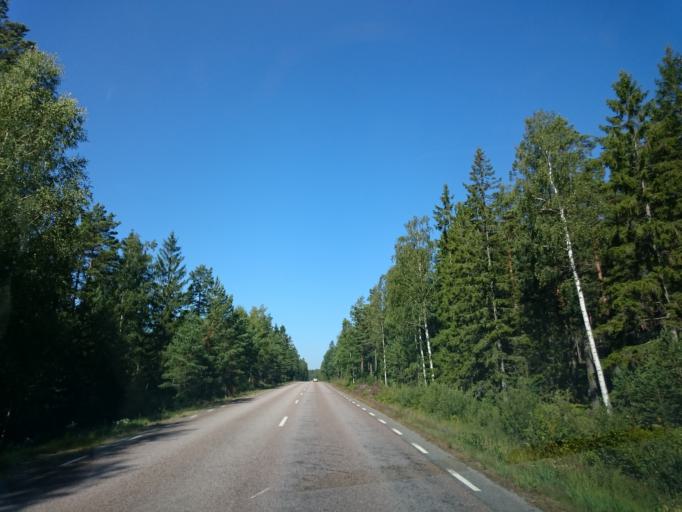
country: SE
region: OEstergoetland
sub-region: Norrkopings Kommun
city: Krokek
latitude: 58.6473
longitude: 16.5707
